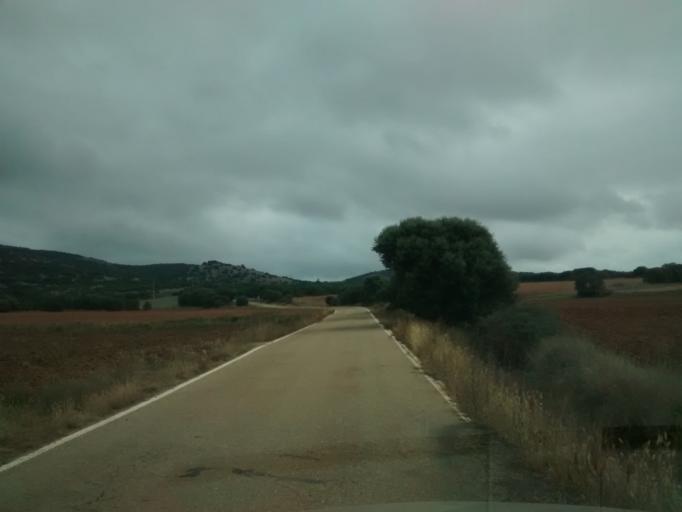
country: ES
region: Aragon
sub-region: Provincia de Zaragoza
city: Gallocanta
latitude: 40.9916
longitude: -1.4818
